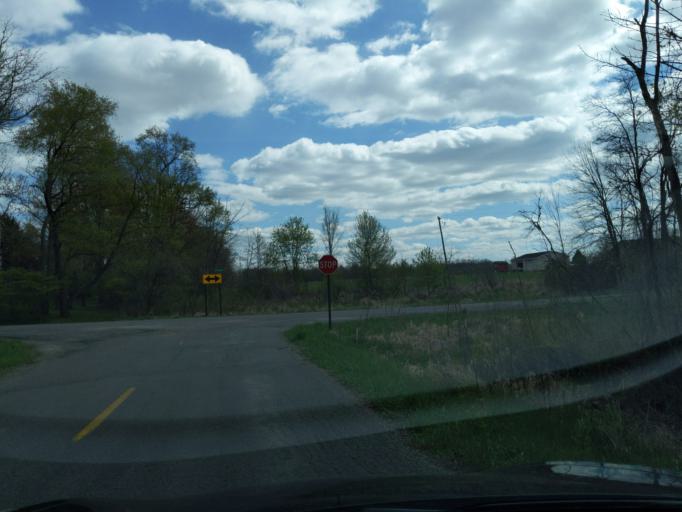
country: US
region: Michigan
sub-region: Eaton County
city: Eaton Rapids
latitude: 42.4877
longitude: -84.5463
